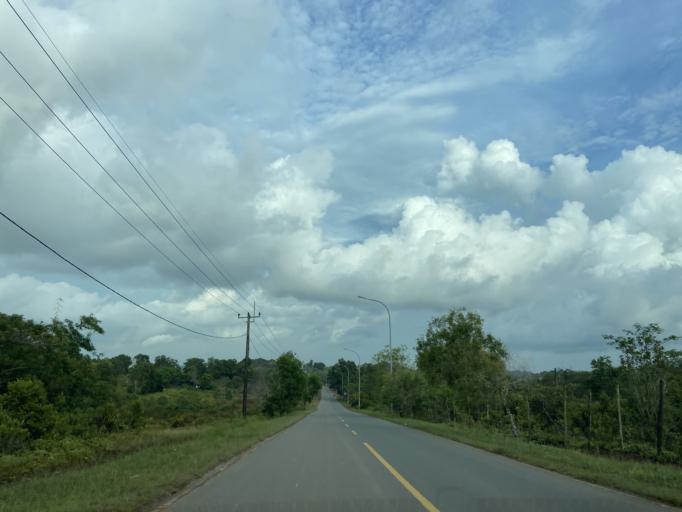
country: ID
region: Riau Islands
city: Tanjungpinang
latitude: 0.9370
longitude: 104.0952
